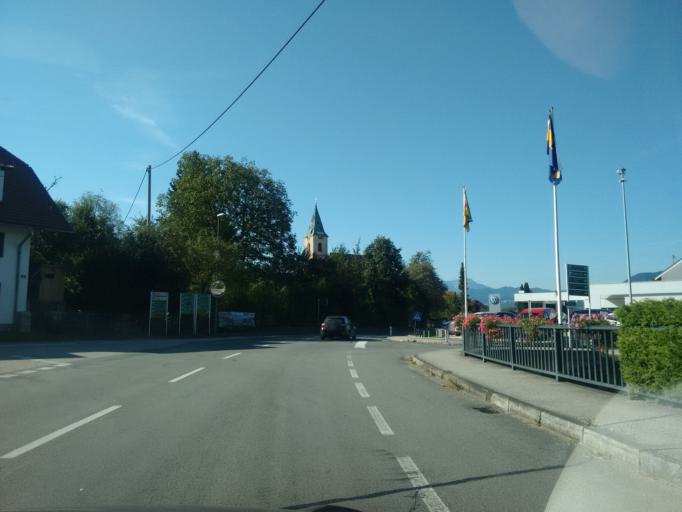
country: AT
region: Upper Austria
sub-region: Politischer Bezirk Vocklabruck
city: Attersee
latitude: 47.9036
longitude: 13.5734
